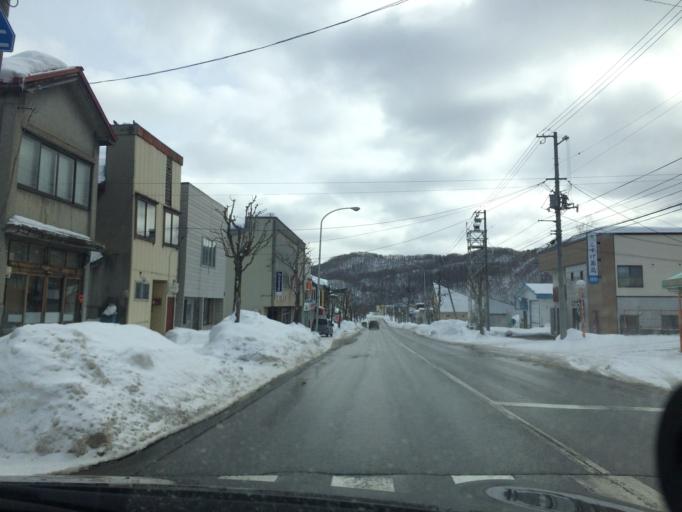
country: JP
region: Hokkaido
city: Iwamizawa
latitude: 43.0252
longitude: 141.9722
